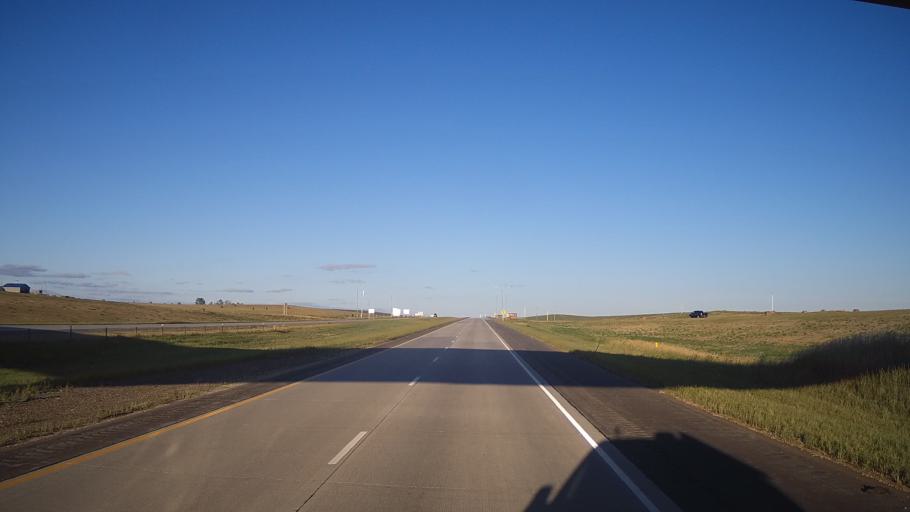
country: US
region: South Dakota
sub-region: Jones County
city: Murdo
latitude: 43.8830
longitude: -100.7059
